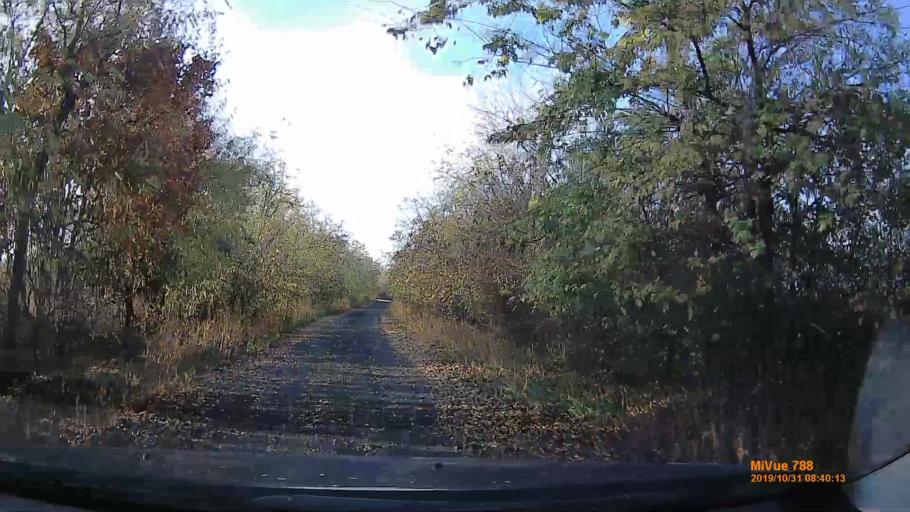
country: HU
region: Pest
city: Pand
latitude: 47.3078
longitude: 19.6477
